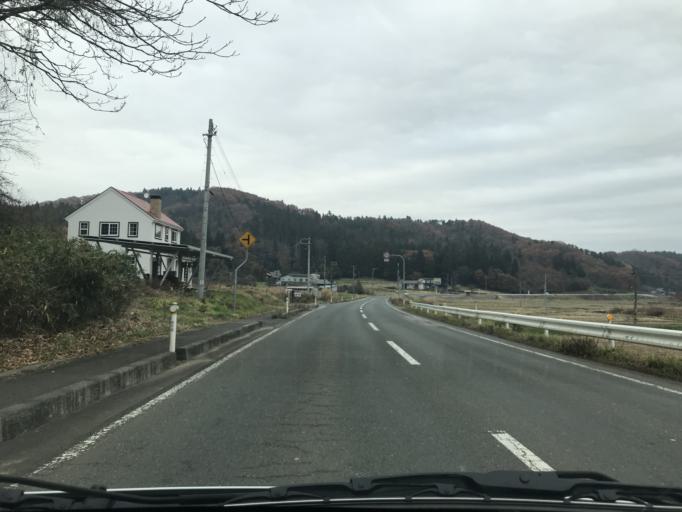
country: JP
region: Iwate
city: Kitakami
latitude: 39.2947
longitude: 141.1771
